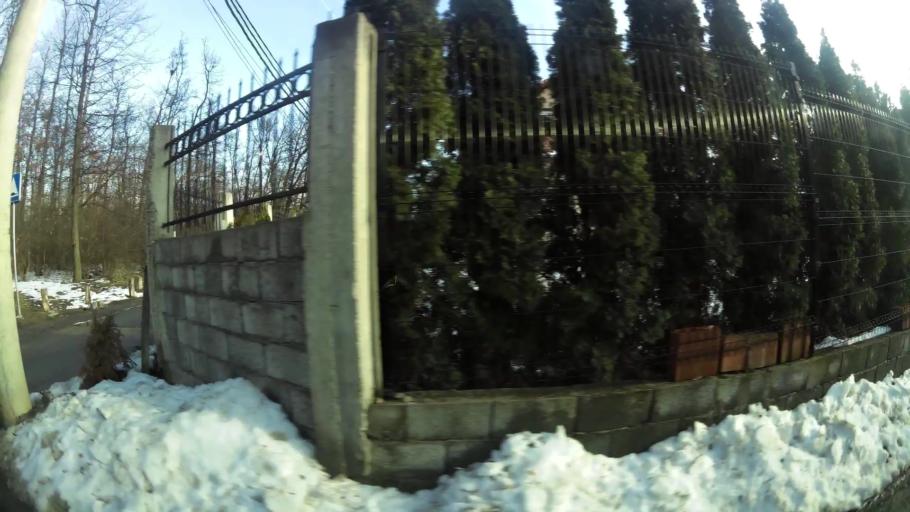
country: RS
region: Central Serbia
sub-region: Belgrade
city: Rakovica
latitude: 44.7388
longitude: 20.4548
